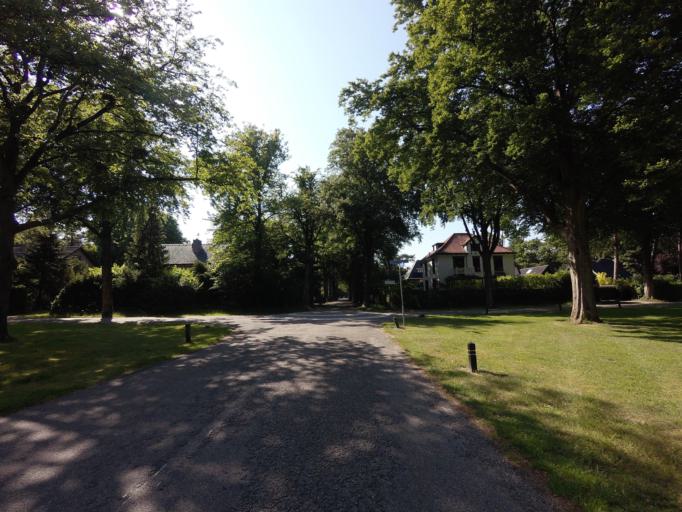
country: NL
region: Utrecht
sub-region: Gemeente De Bilt
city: De Bilt
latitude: 52.1332
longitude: 5.2061
